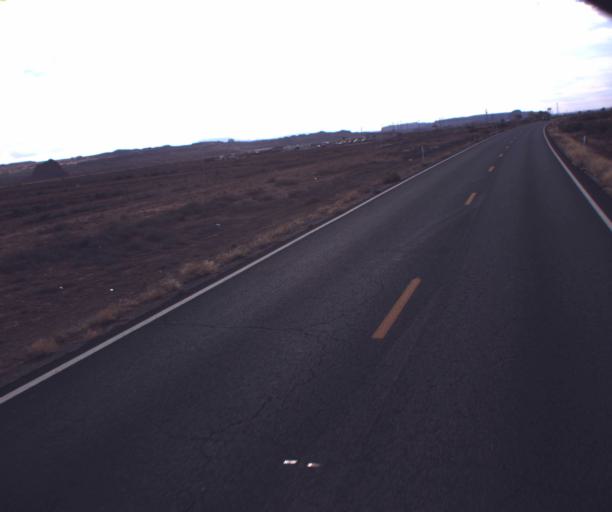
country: US
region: Arizona
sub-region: Apache County
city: Many Farms
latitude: 36.7389
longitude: -109.6357
